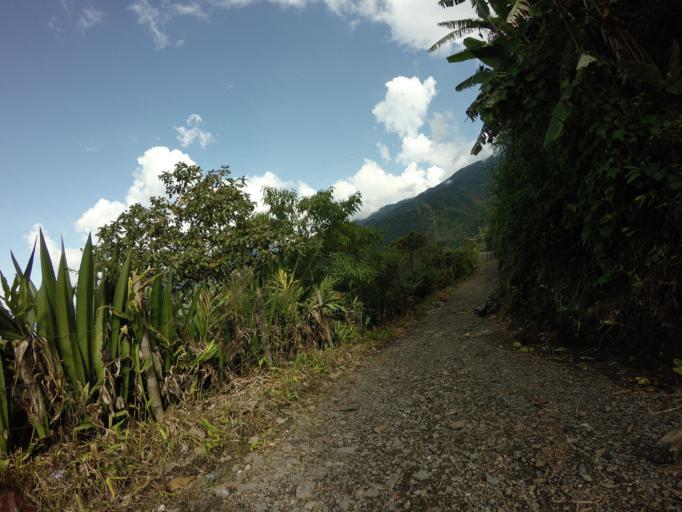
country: CO
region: Caldas
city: Pensilvania
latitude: 5.4624
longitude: -75.1682
